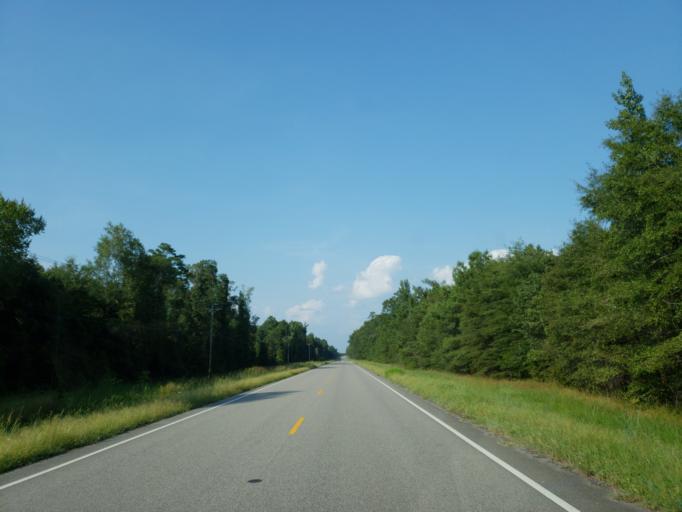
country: US
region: Alabama
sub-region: Sumter County
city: Livingston
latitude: 32.7335
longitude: -88.0579
